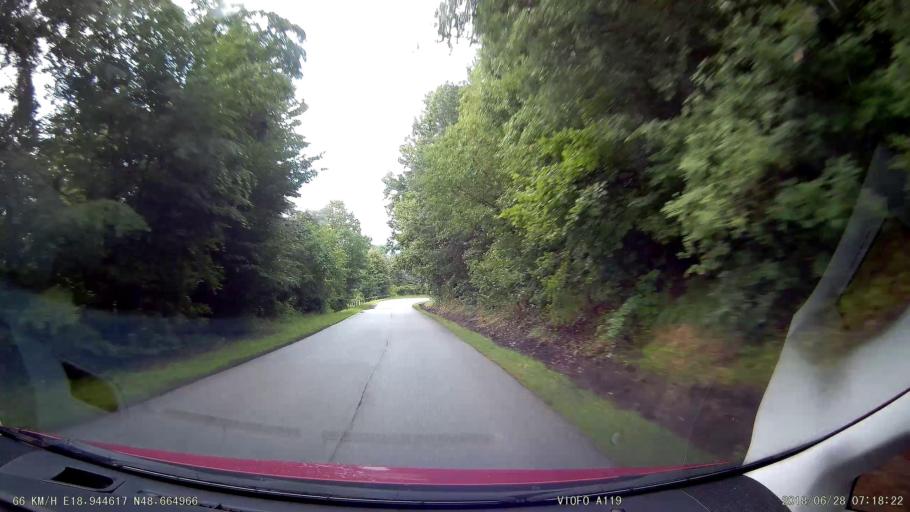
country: SK
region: Banskobystricky
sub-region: Okres Ziar nad Hronom
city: Kremnica
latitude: 48.6647
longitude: 18.9447
